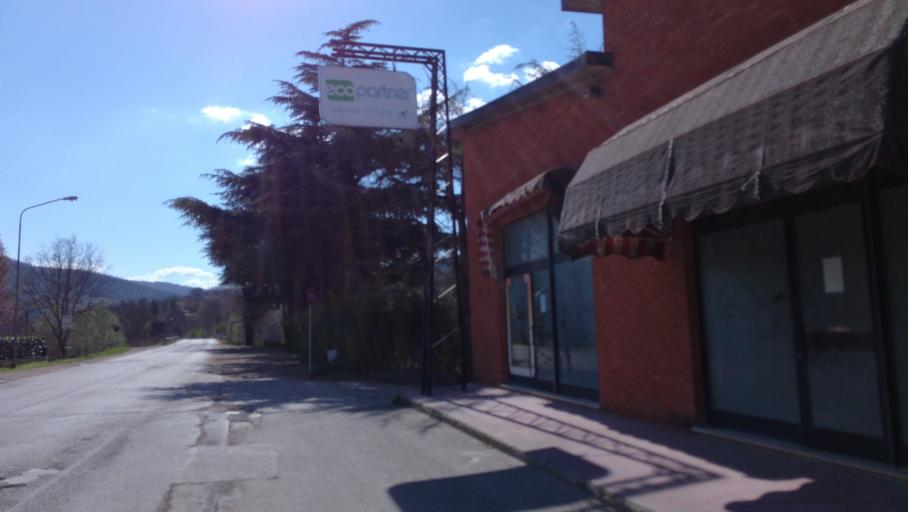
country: IT
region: Umbria
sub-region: Provincia di Perugia
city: Trestina
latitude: 43.3450
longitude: 12.2211
